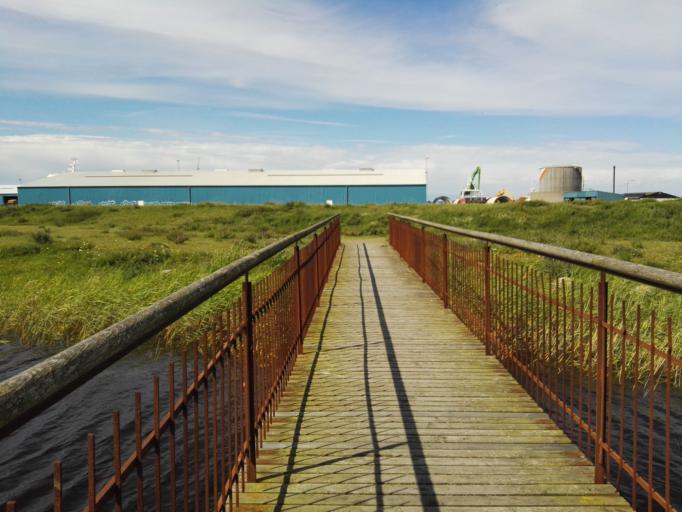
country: DK
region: Capital Region
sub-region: Halsnaes Kommune
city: Hundested
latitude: 55.9604
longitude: 11.8506
